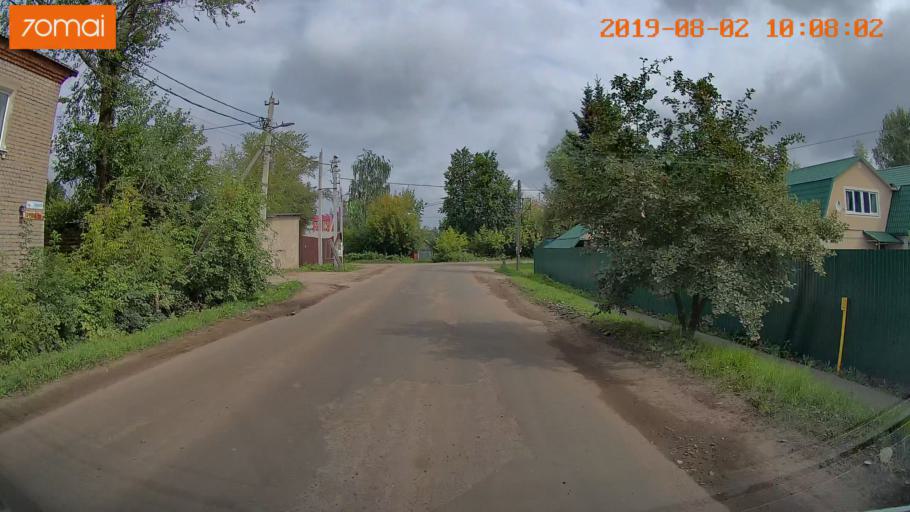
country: RU
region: Ivanovo
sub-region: Gorod Ivanovo
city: Ivanovo
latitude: 56.9850
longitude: 40.9369
